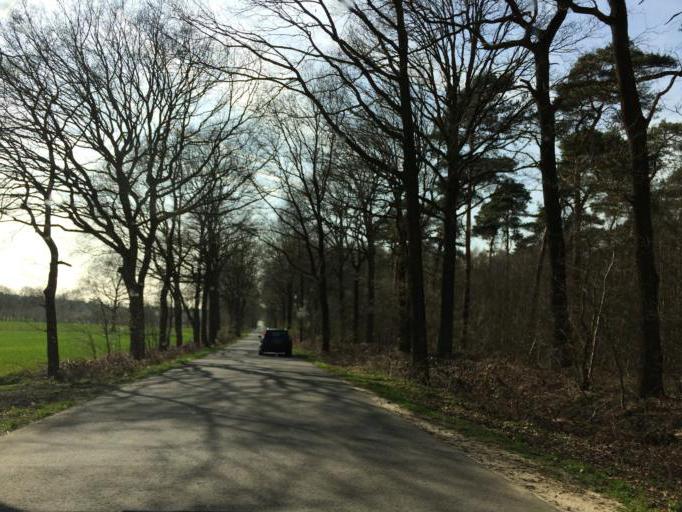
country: DE
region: North Rhine-Westphalia
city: Marl
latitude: 51.7154
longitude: 7.0610
